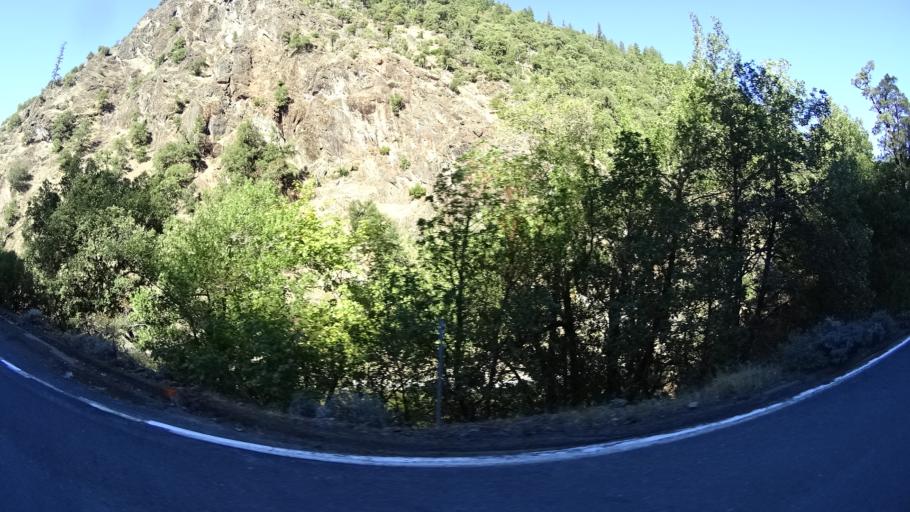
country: US
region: California
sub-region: Siskiyou County
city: Happy Camp
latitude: 41.3747
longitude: -123.4264
